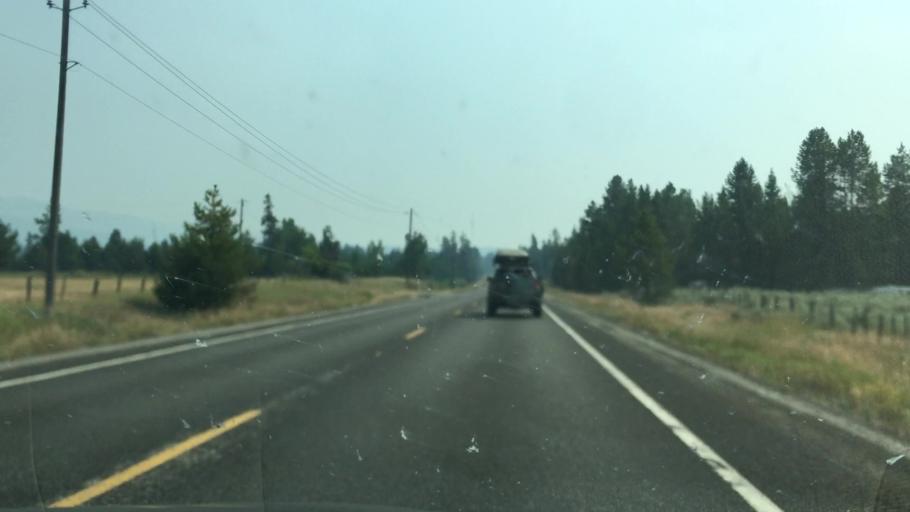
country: US
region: Idaho
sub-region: Valley County
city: Cascade
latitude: 44.4150
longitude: -115.9998
